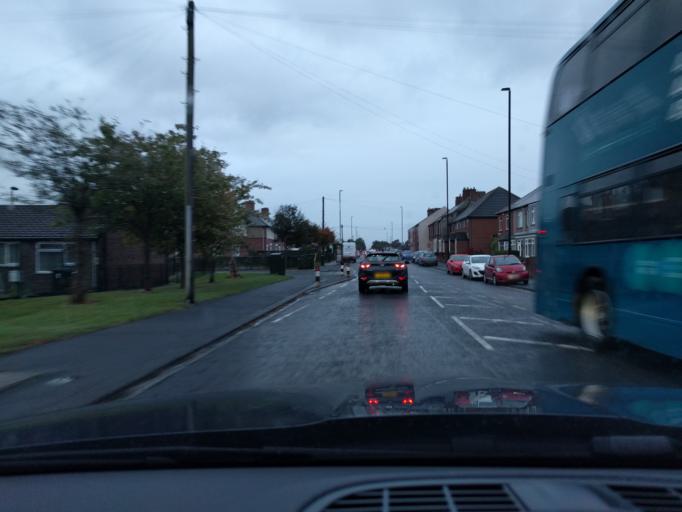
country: GB
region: England
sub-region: Northumberland
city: Backworth
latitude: 55.0251
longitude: -1.5486
